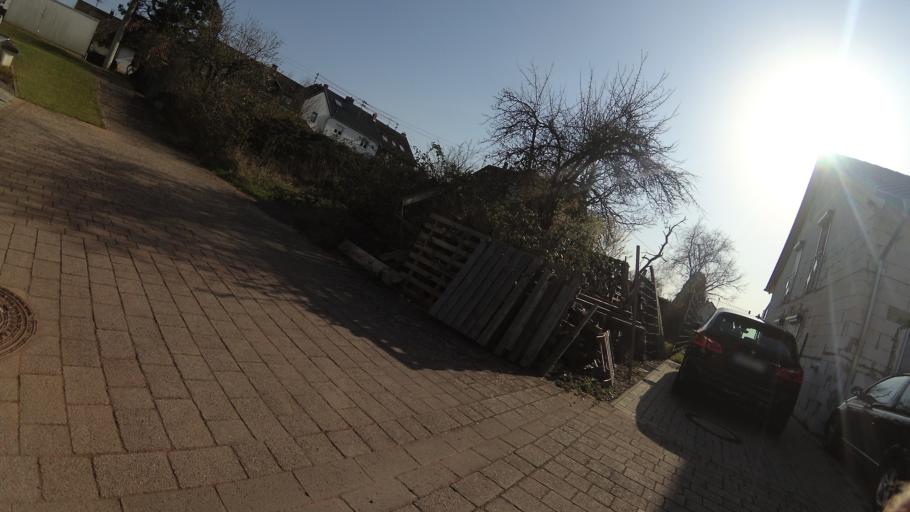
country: DE
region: Saarland
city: Heusweiler
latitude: 49.3332
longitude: 6.9292
